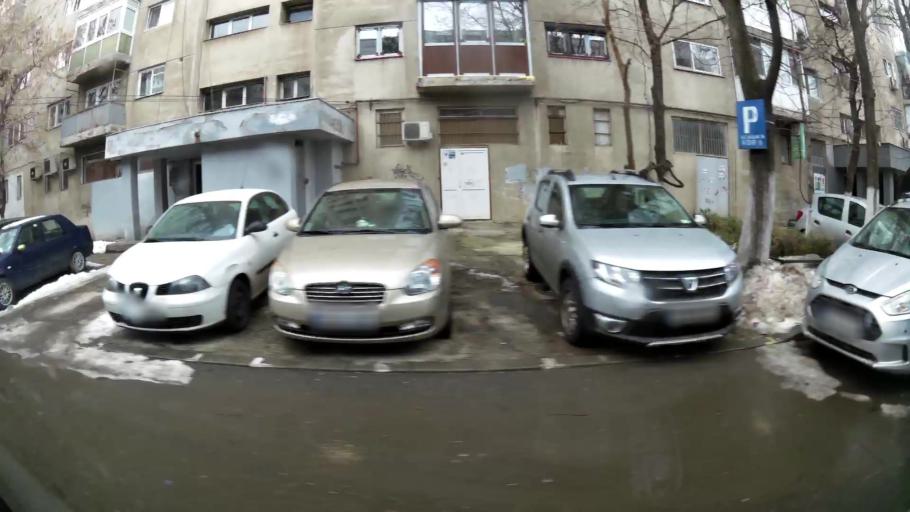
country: RO
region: Ilfov
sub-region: Comuna Chiajna
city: Rosu
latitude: 44.4168
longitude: 26.0336
